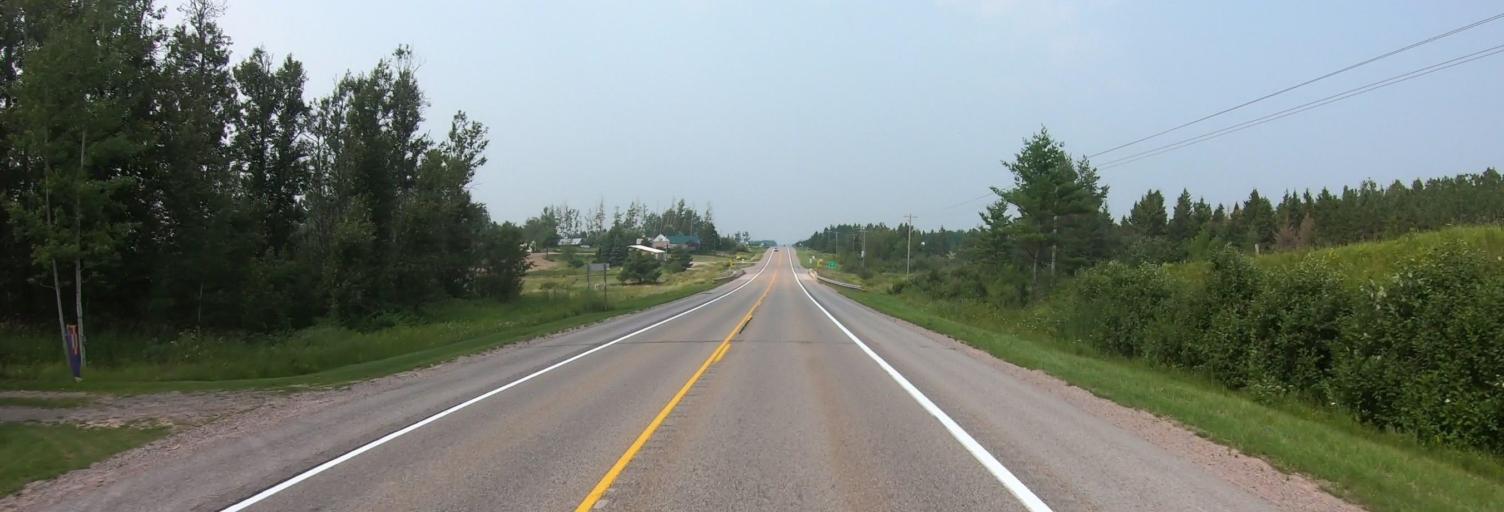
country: US
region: Michigan
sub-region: Chippewa County
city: Sault Ste. Marie
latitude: 46.3331
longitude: -84.3640
